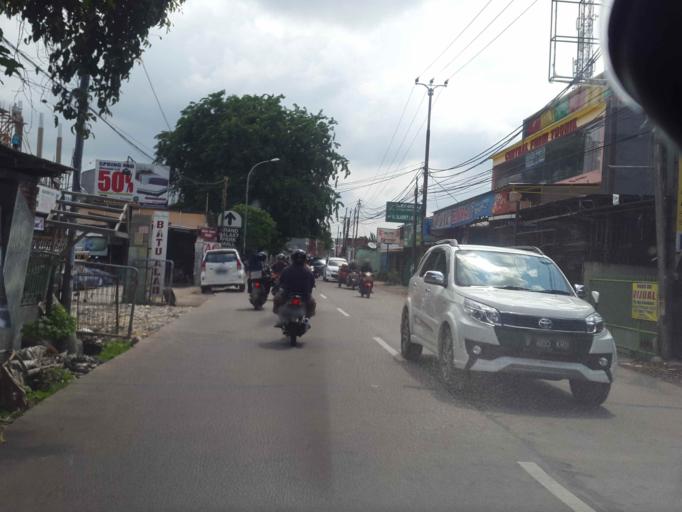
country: ID
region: West Java
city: Bekasi
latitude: -6.2698
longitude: 106.9812
